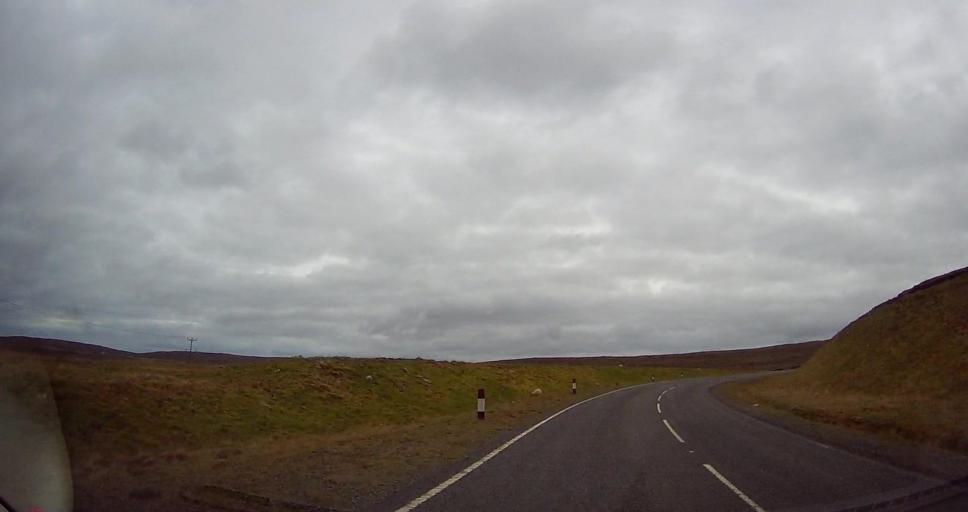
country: GB
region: Scotland
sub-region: Shetland Islands
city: Shetland
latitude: 60.6488
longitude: -1.0668
